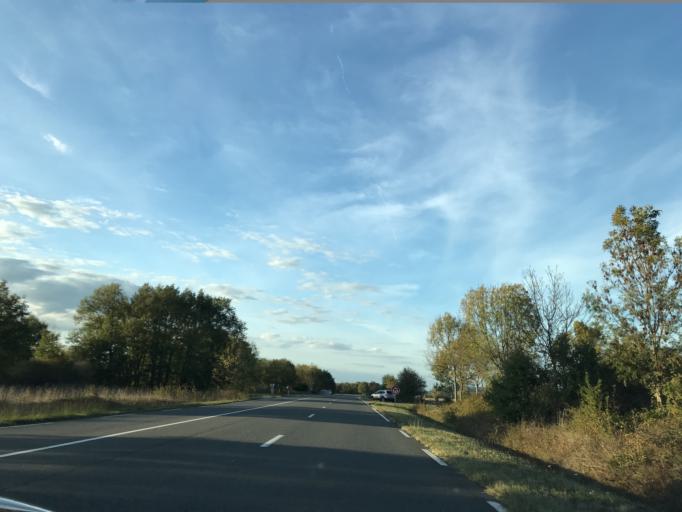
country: FR
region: Auvergne
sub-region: Departement de l'Allier
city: Saint-Yorre
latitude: 46.0204
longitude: 3.4812
